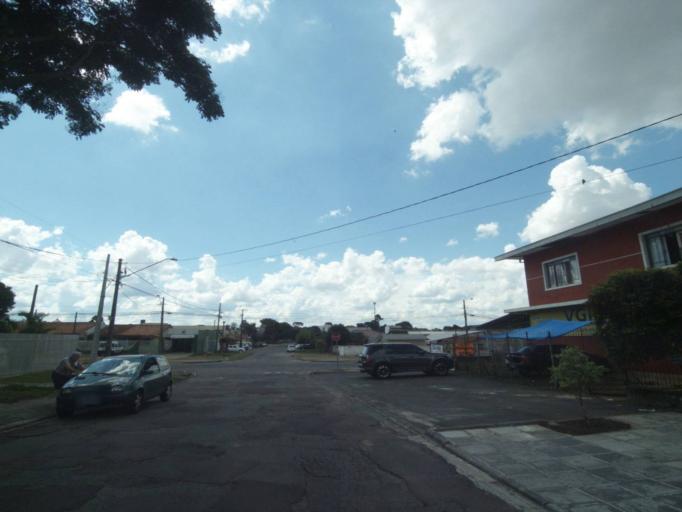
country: BR
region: Parana
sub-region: Pinhais
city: Pinhais
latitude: -25.4582
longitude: -49.2089
